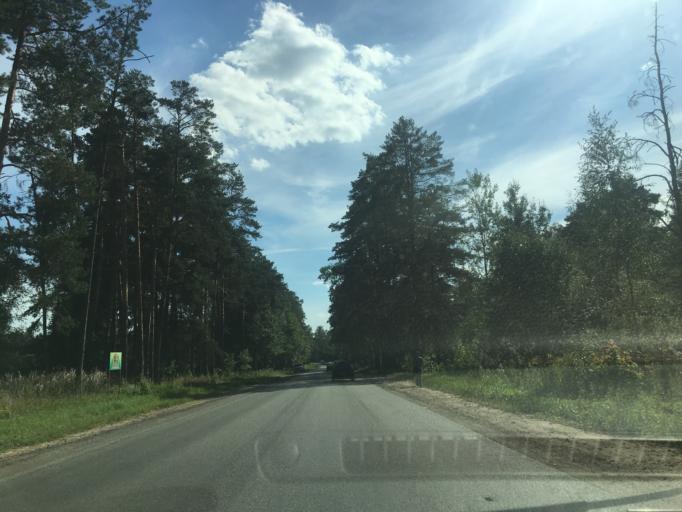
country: RU
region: Moscow
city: Zagor'ye
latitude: 55.5307
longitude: 37.6640
